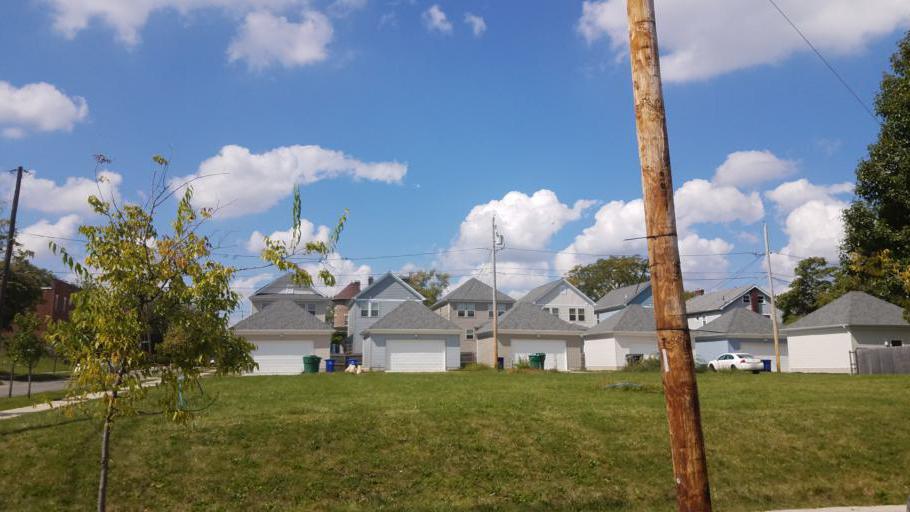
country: US
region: Ohio
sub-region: Franklin County
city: Columbus
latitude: 39.9918
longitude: -82.9993
